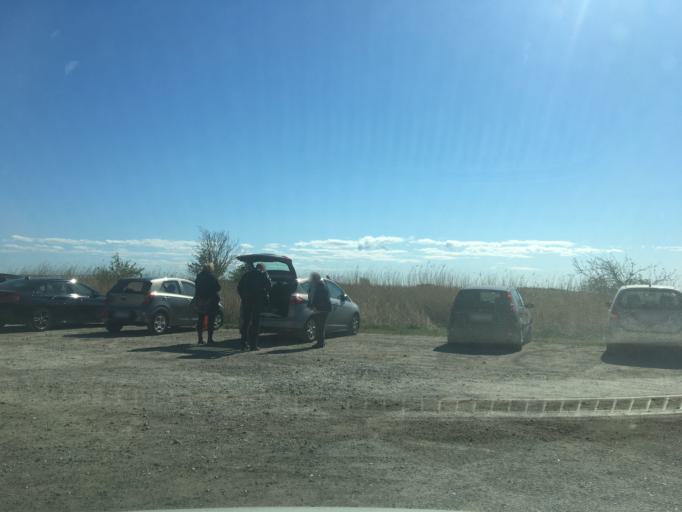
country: DK
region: Capital Region
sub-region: Dragor Kommune
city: Dragor
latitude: 55.5821
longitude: 12.6584
